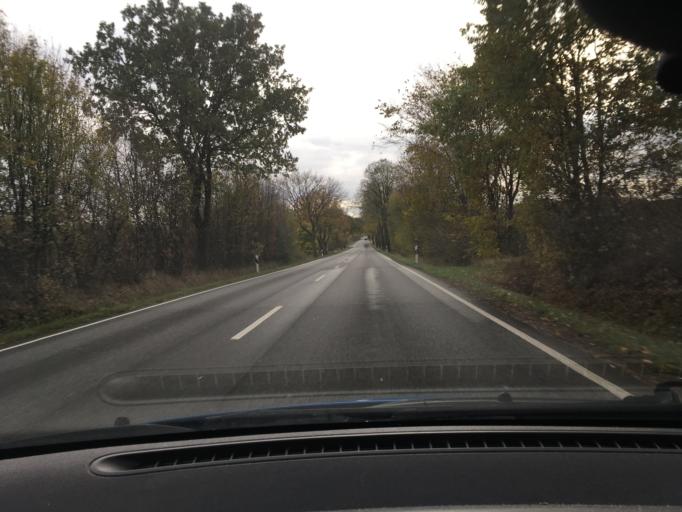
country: DE
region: Schleswig-Holstein
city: Talkau
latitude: 53.5734
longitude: 10.5672
